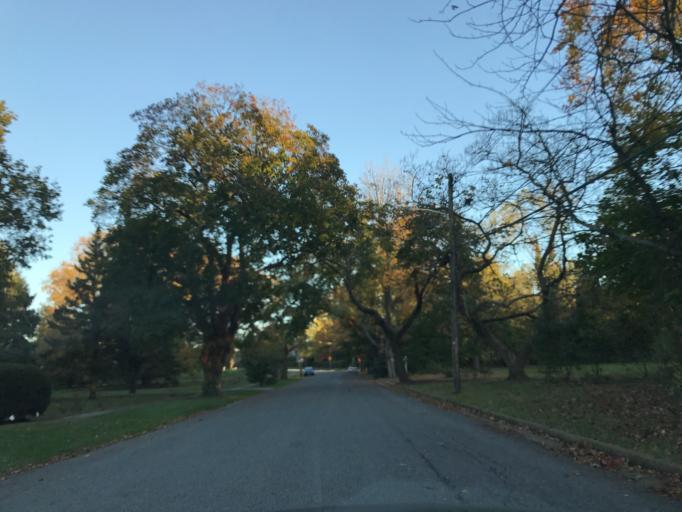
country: US
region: Maryland
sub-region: Baltimore County
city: Lutherville
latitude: 39.4237
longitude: -76.6222
